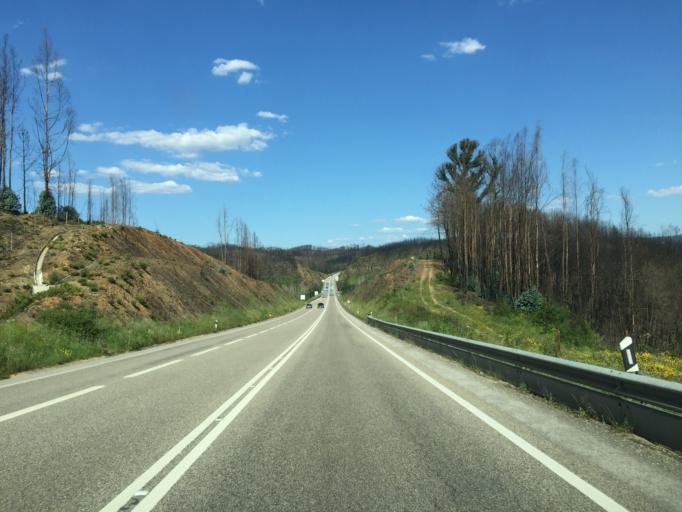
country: PT
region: Leiria
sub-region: Pedrogao Grande
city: Pedrogao Grande
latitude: 39.9263
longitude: -8.1962
